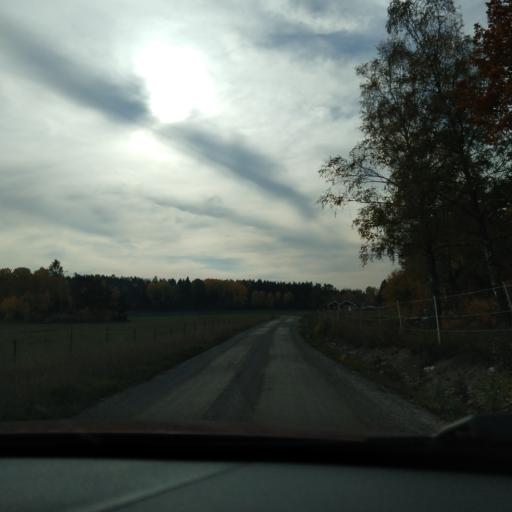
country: SE
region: Stockholm
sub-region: Vallentuna Kommun
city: Vallentuna
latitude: 59.5349
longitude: 18.0138
